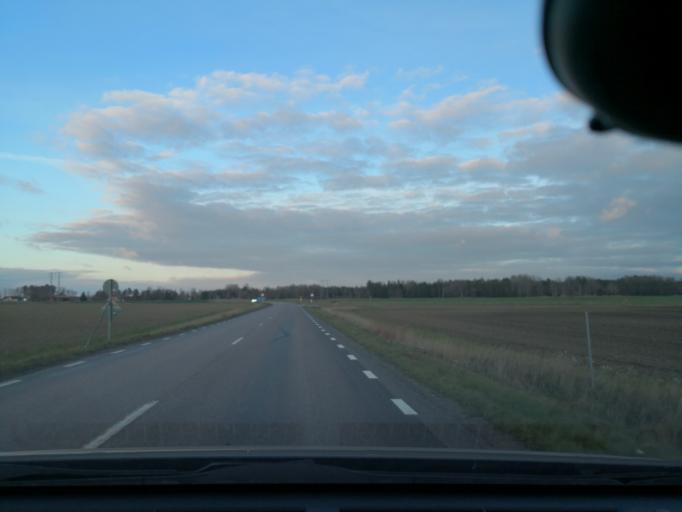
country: SE
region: Vaestmanland
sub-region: Vasteras
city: Tillberga
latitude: 59.6515
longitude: 16.6888
